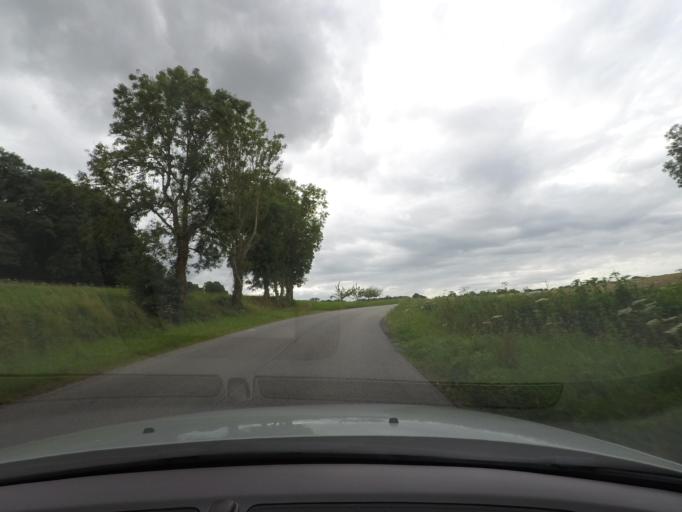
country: FR
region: Haute-Normandie
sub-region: Departement de l'Eure
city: Les Andelys
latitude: 49.2569
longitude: 1.3737
